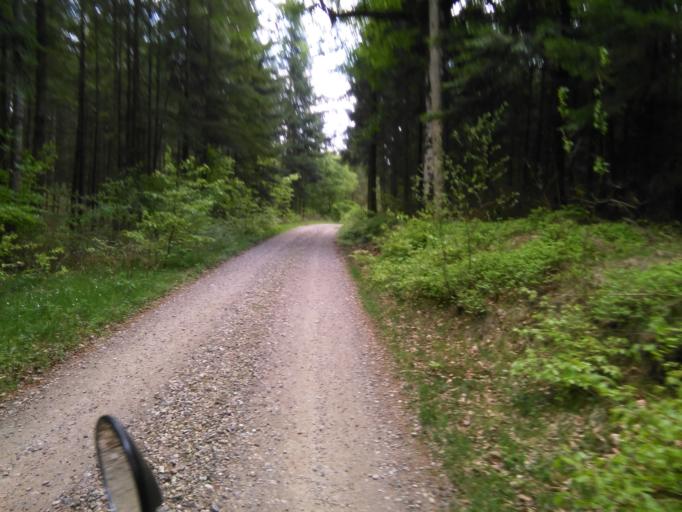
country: DK
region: Central Jutland
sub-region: Horsens Kommune
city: Braedstrup
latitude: 56.0500
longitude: 9.6116
